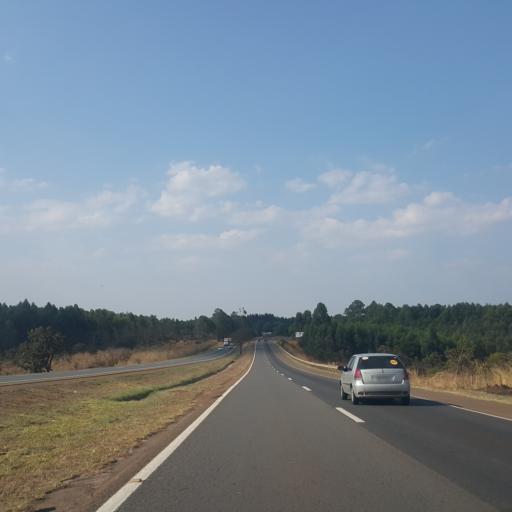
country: BR
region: Goias
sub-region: Abadiania
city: Abadiania
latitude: -16.1886
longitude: -48.7006
